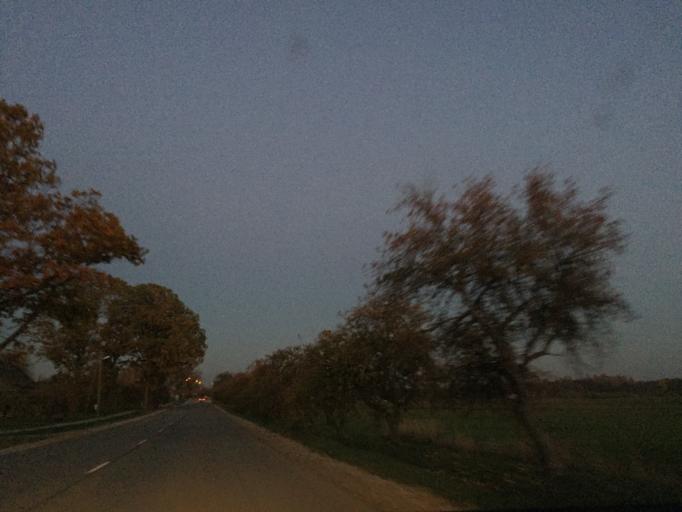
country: LT
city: Zagare
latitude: 56.4845
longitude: 23.1824
